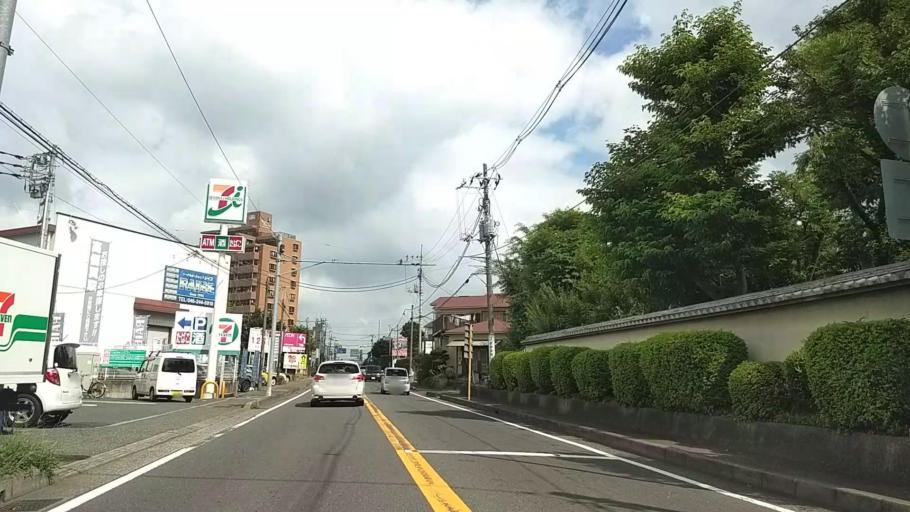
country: JP
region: Kanagawa
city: Minami-rinkan
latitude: 35.5014
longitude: 139.4668
